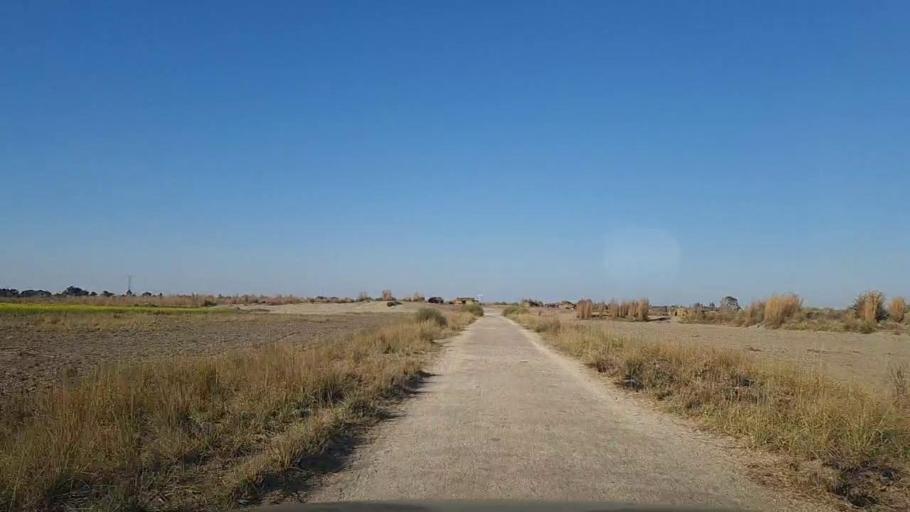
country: PK
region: Sindh
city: Khadro
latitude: 26.2456
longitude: 68.8629
